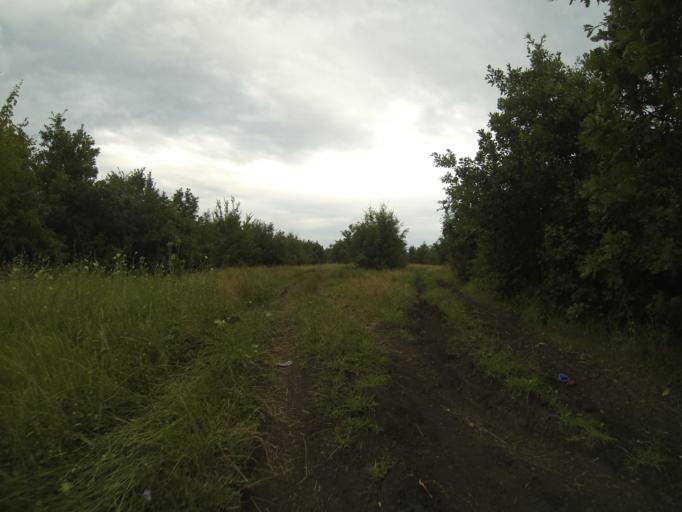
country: RO
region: Dolj
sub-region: Comuna Filiasi
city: Fratostita
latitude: 44.5792
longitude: 23.6126
